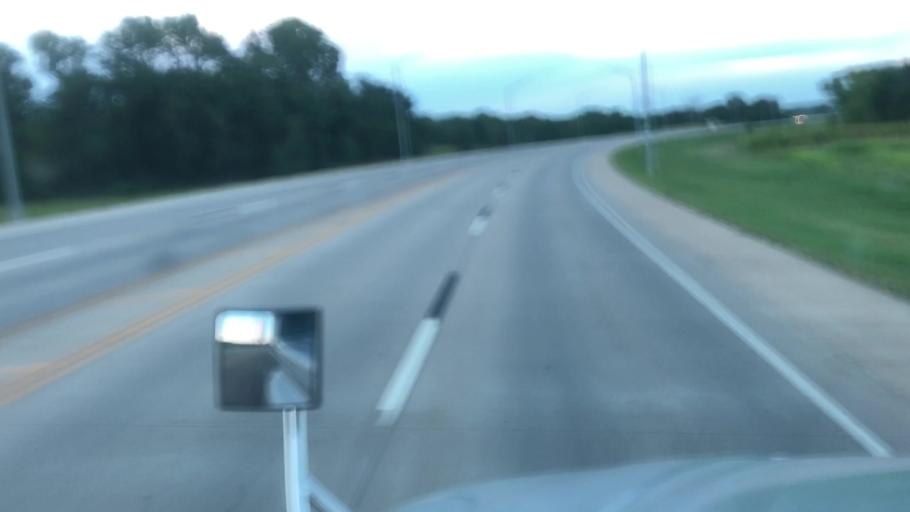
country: US
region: Oklahoma
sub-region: Kay County
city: Ponca City
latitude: 36.6834
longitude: -97.0700
